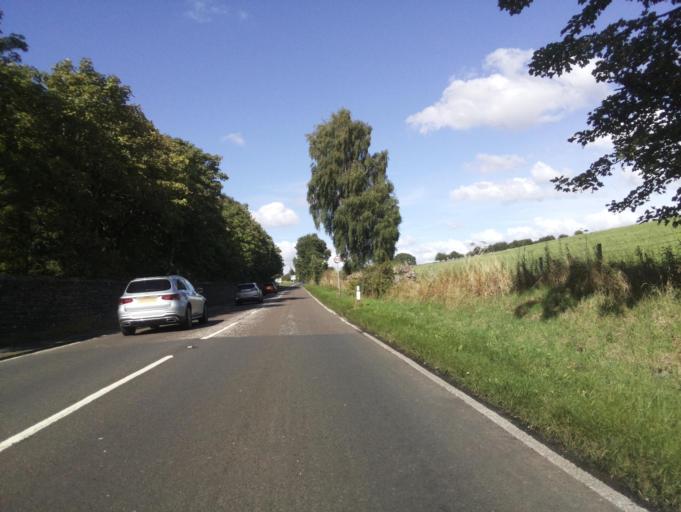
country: GB
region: Scotland
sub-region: Stirling
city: Dunblane
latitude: 56.1663
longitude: -3.9693
